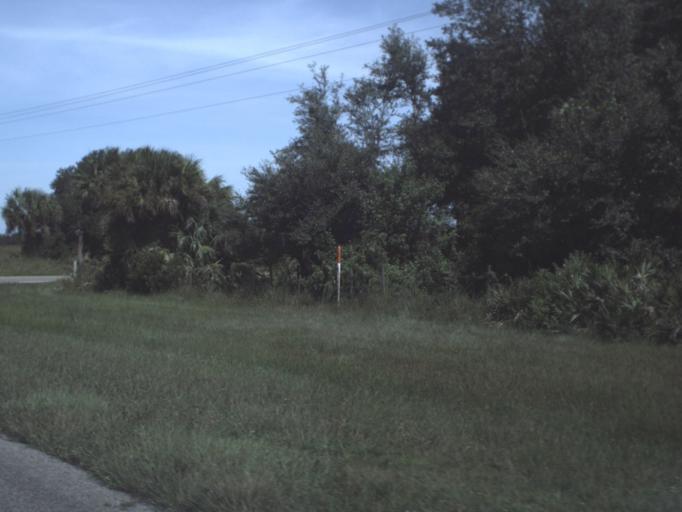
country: US
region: Florida
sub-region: Hendry County
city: Port LaBelle
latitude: 26.9729
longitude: -81.3176
